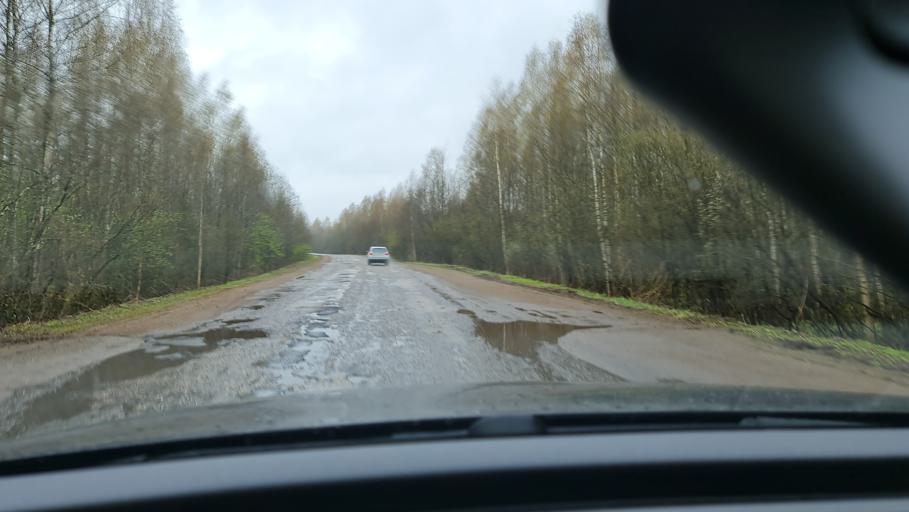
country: RU
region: Novgorod
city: Kresttsy
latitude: 57.9659
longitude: 32.7097
